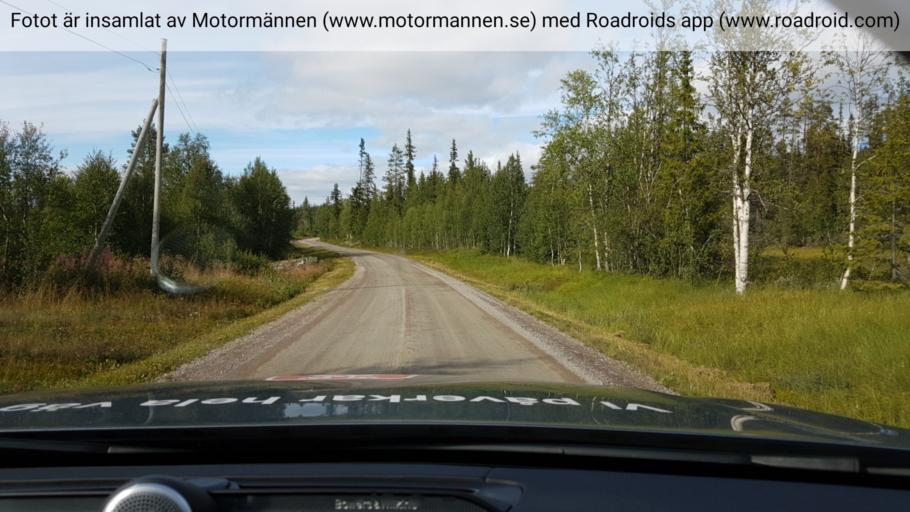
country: SE
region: Jaemtland
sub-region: Stroemsunds Kommun
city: Stroemsund
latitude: 64.5209
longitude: 15.1095
